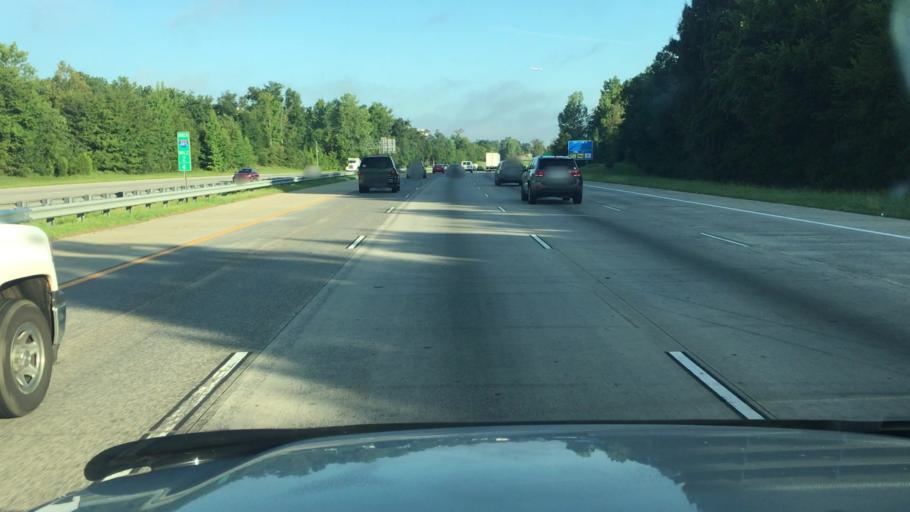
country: US
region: North Carolina
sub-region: Mecklenburg County
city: Pineville
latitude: 35.1478
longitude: -80.9411
